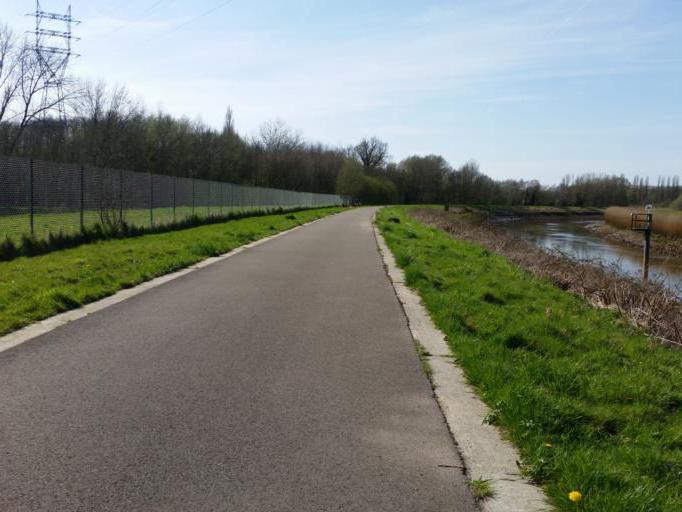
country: BE
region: Flanders
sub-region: Provincie Antwerpen
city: Mechelen
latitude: 51.0353
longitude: 4.4610
